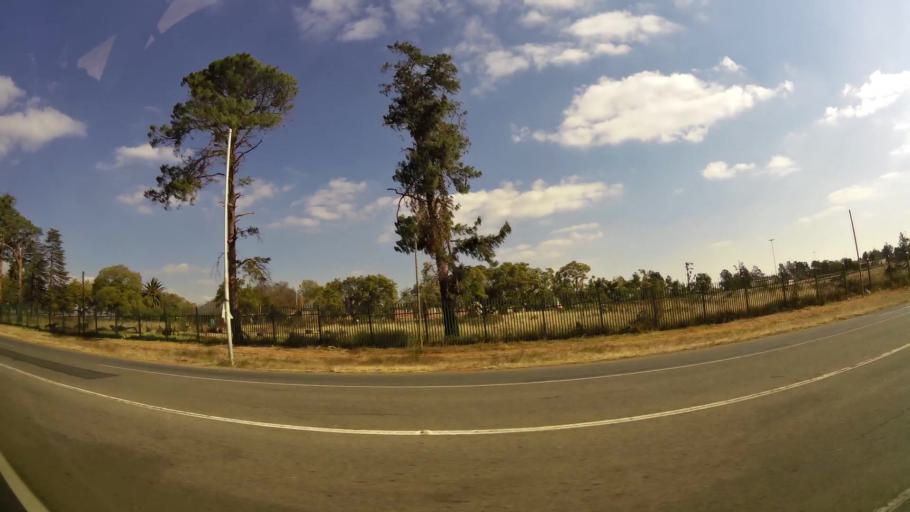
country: ZA
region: Gauteng
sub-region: West Rand District Municipality
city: Krugersdorp
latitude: -26.0602
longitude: 27.7576
